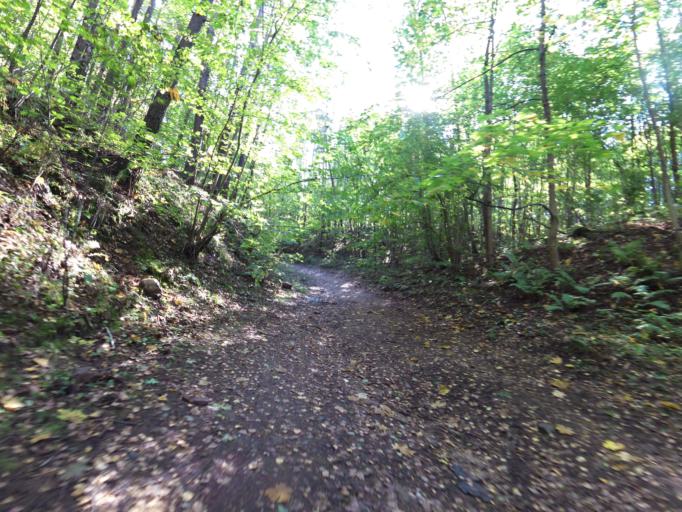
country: LT
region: Vilnius County
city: Pilaite
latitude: 54.6889
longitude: 25.1921
